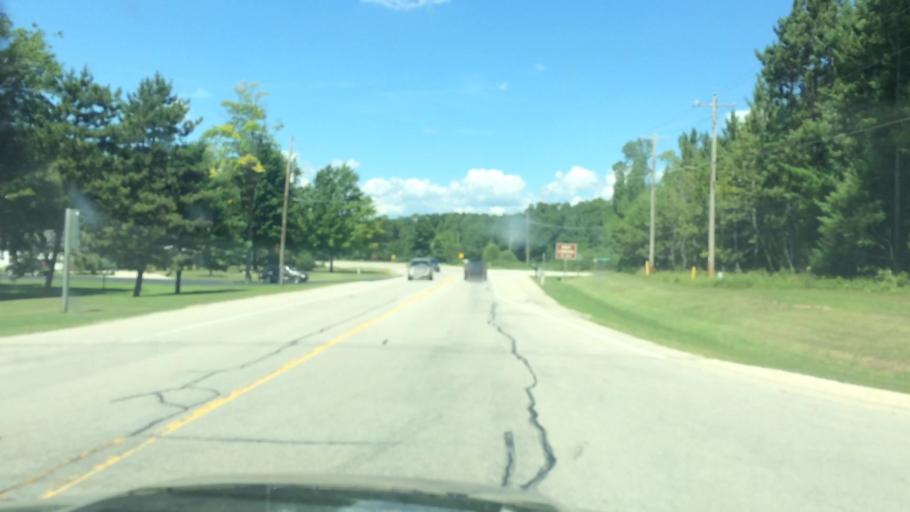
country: US
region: Wisconsin
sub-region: Marinette County
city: Peshtigo
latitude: 45.1050
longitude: -87.7503
